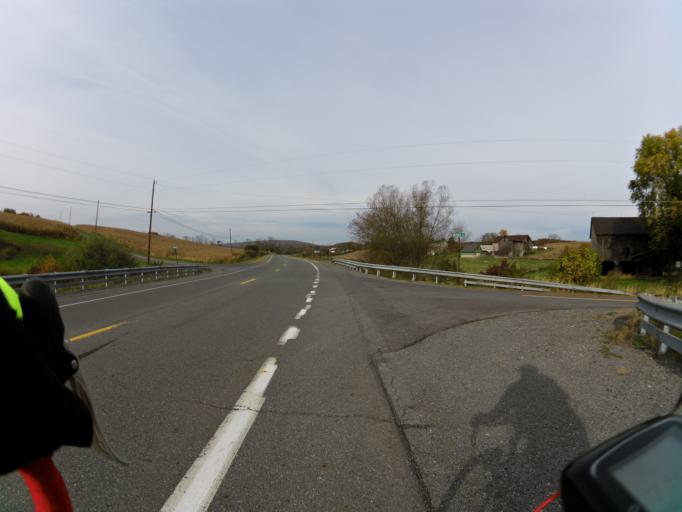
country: US
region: Pennsylvania
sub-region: Union County
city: New Columbia
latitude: 41.0525
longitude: -76.8891
